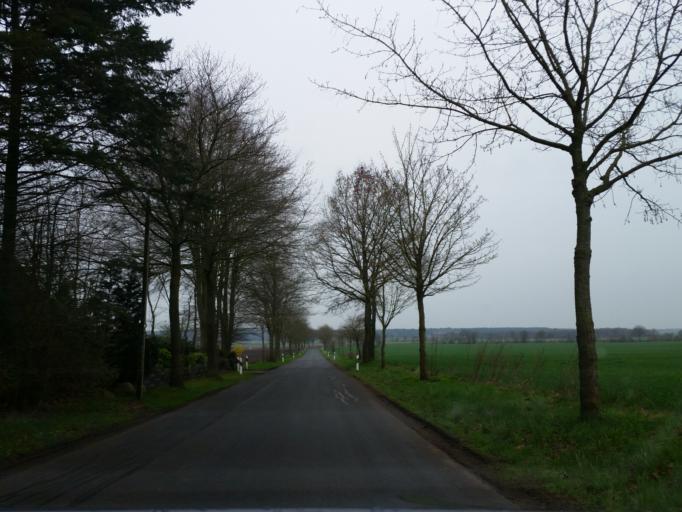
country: DE
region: Lower Saxony
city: Alfstedt
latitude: 53.5730
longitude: 9.0674
